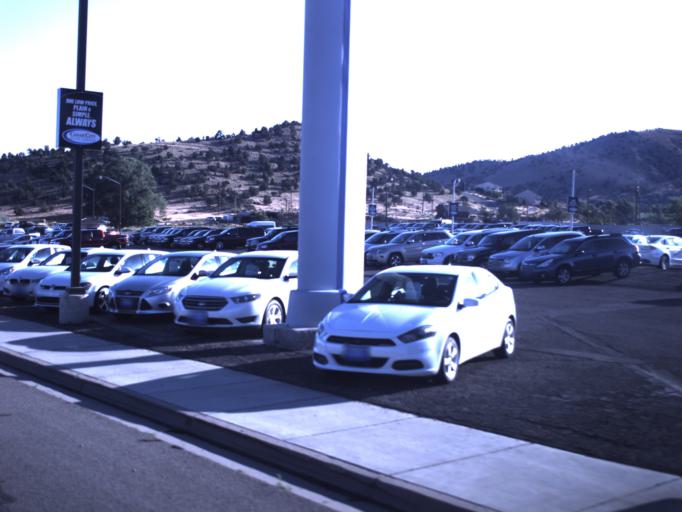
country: US
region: Utah
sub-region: Iron County
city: Cedar City
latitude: 37.6942
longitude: -113.0624
